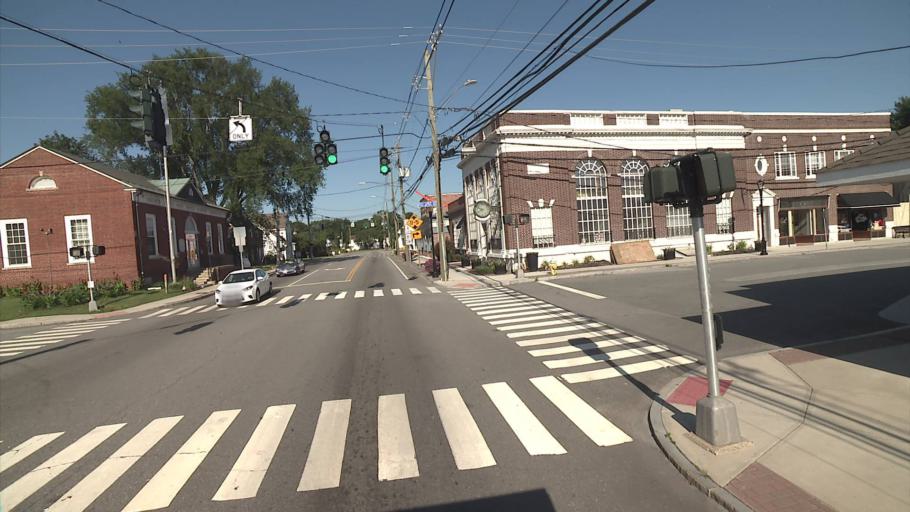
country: US
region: Connecticut
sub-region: Middlesex County
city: Clinton
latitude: 41.2786
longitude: -72.5270
